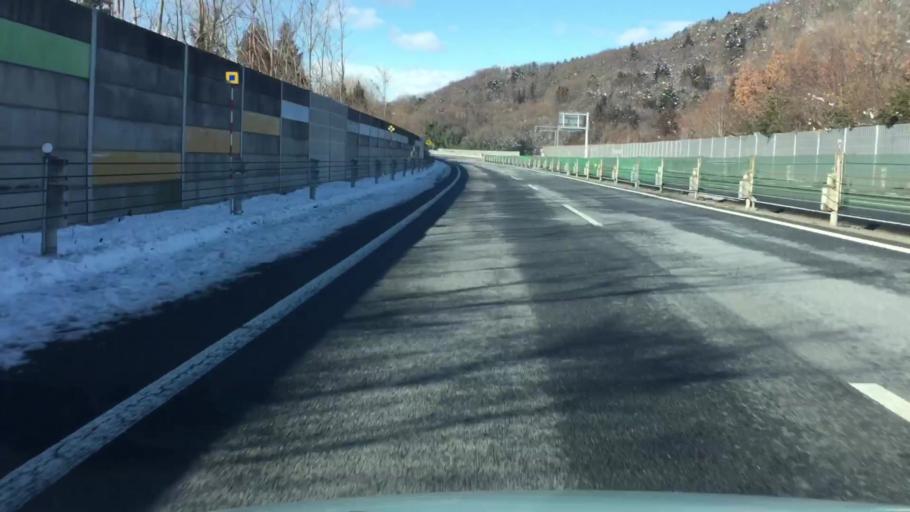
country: JP
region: Gunma
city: Numata
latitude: 36.6716
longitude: 139.0436
